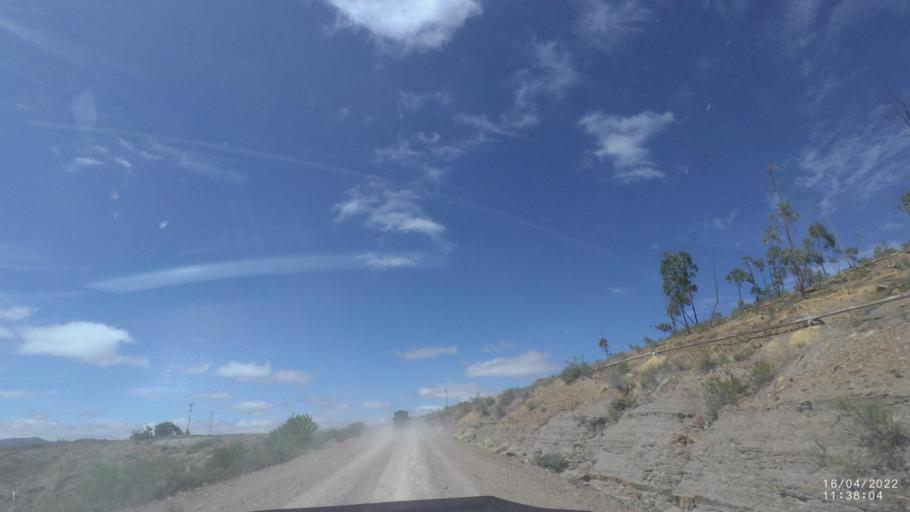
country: BO
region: Cochabamba
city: Mizque
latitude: -17.9630
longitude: -65.6404
